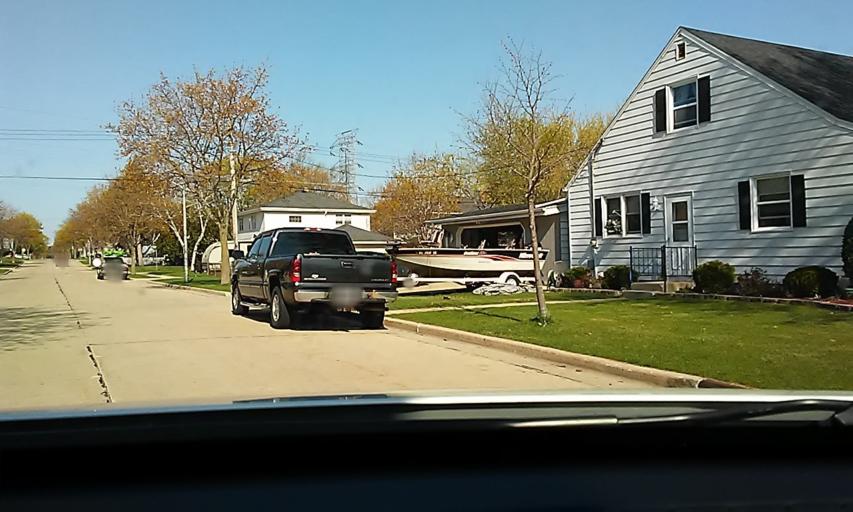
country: US
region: Wisconsin
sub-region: Waukesha County
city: Elm Grove
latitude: 43.0182
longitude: -88.0497
